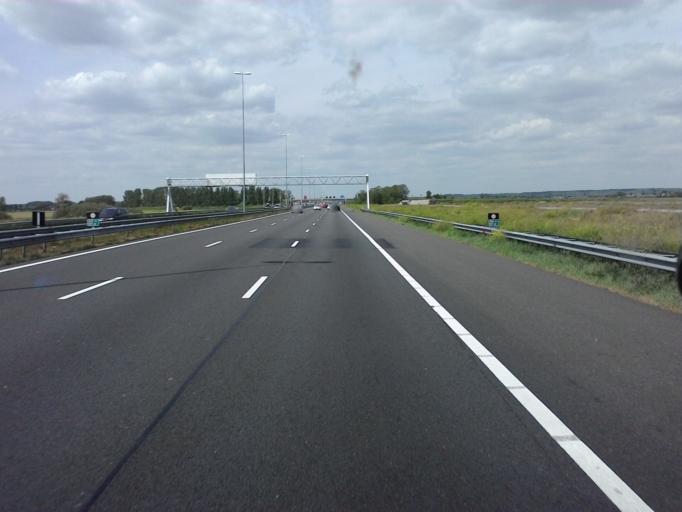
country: NL
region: Gelderland
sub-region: Gemeente Overbetuwe
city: Valburg
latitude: 51.9258
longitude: 5.7705
